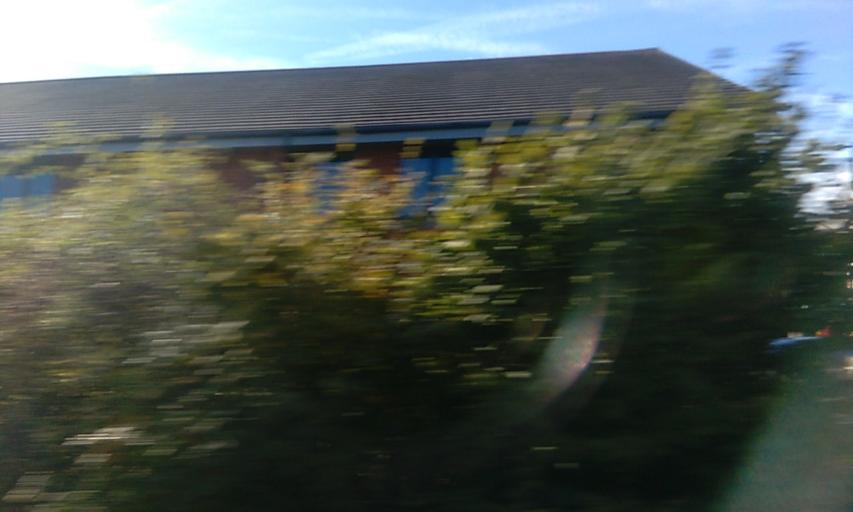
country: GB
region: England
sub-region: Leicestershire
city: Loughborough
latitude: 52.7828
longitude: -1.2024
